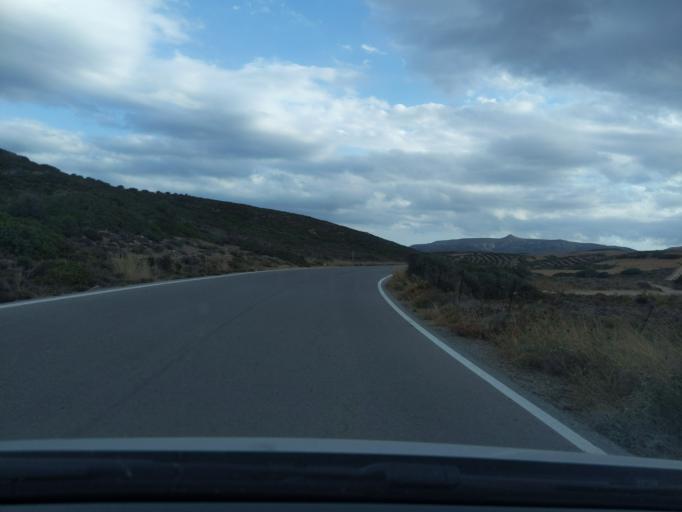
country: GR
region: Crete
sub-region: Nomos Lasithiou
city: Palekastro
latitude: 35.2350
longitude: 26.2518
